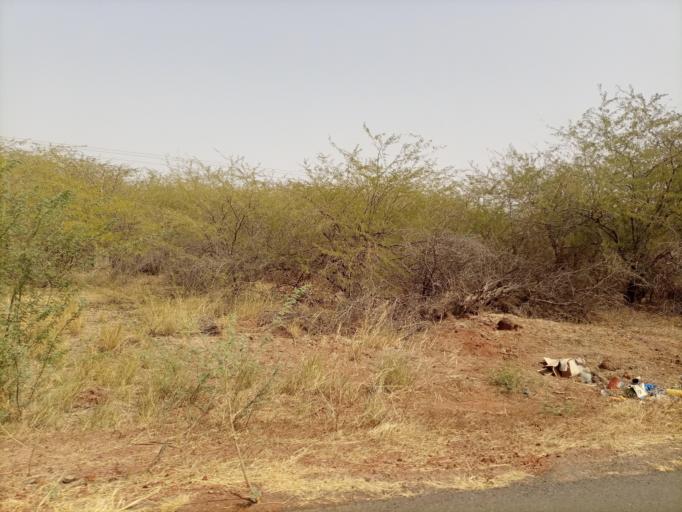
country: SN
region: Fatick
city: Foundiougne
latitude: 14.1769
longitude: -16.4584
